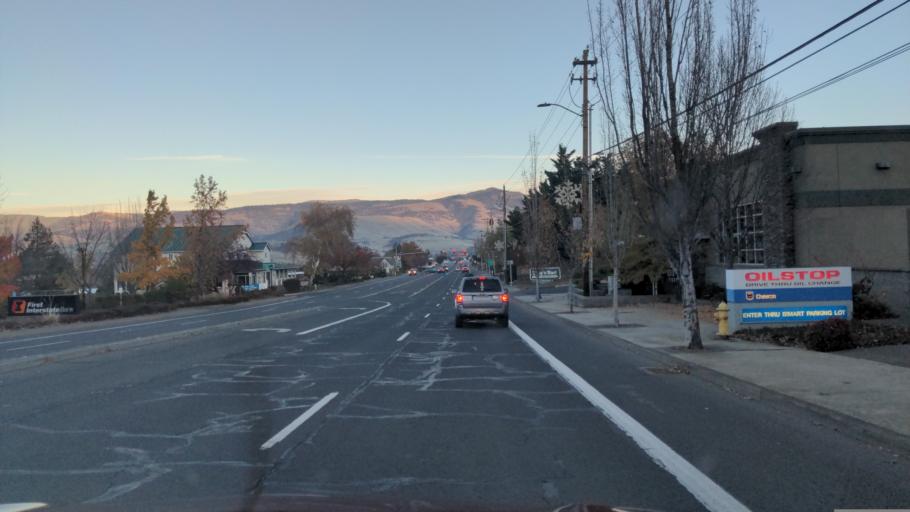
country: US
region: Oregon
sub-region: Jackson County
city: Ashland
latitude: 42.1853
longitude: -122.6744
